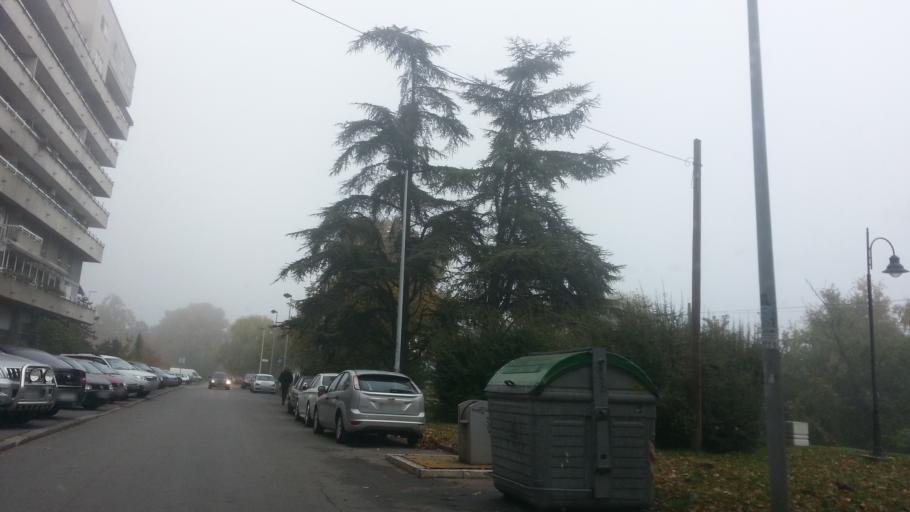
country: RS
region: Central Serbia
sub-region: Belgrade
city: Zemun
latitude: 44.8381
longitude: 20.4186
